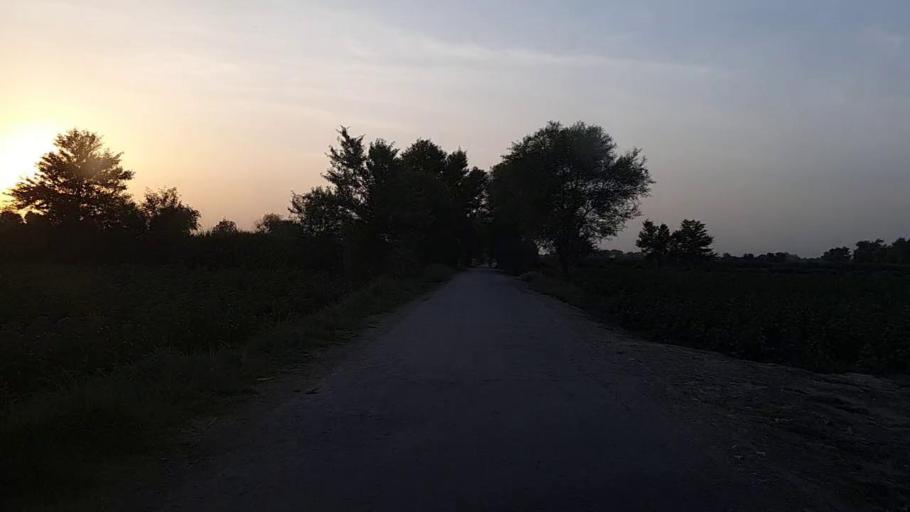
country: PK
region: Sindh
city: Ubauro
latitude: 28.3007
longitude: 69.7962
